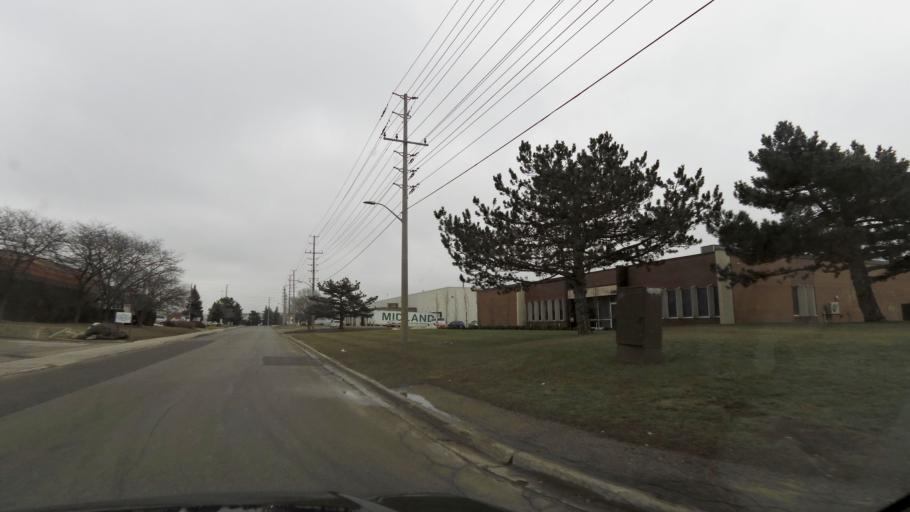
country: CA
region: Ontario
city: Etobicoke
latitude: 43.7008
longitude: -79.6171
